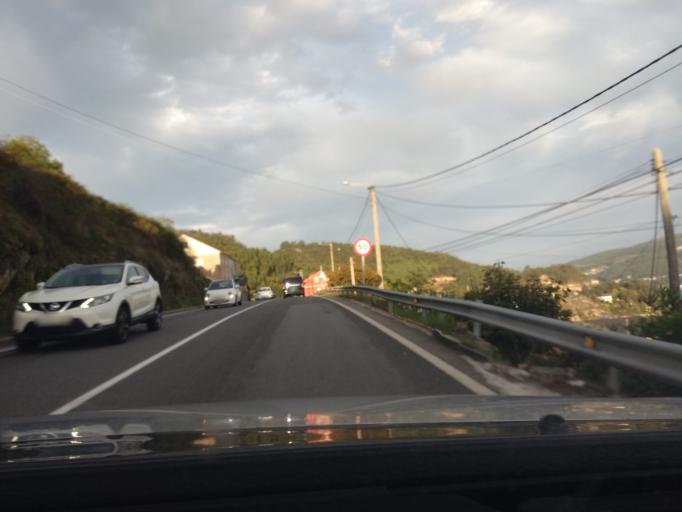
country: ES
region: Galicia
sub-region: Provincia de Pontevedra
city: Moana
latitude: 42.2814
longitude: -8.7087
